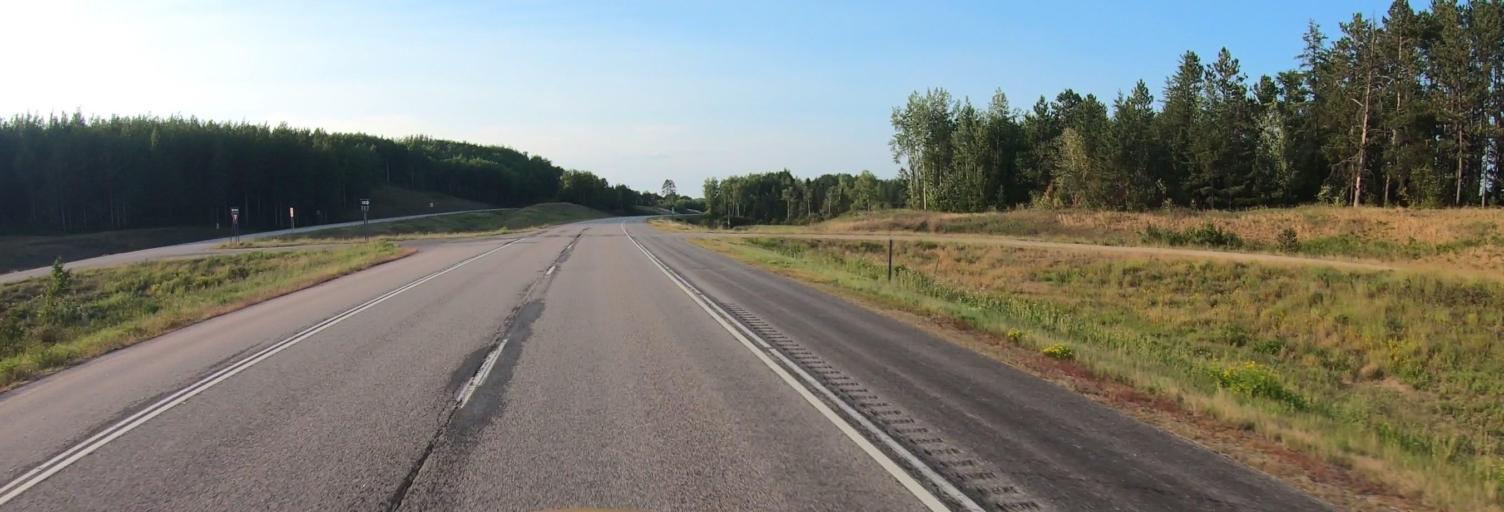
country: US
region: Minnesota
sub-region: Saint Louis County
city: Mountain Iron
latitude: 47.6806
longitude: -92.6374
